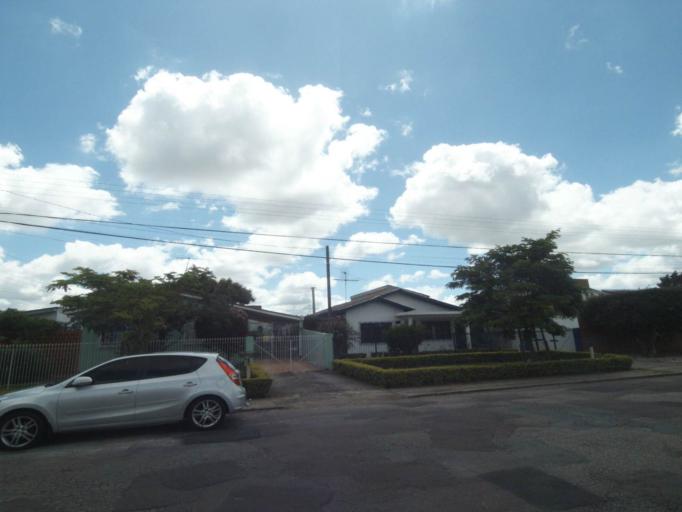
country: BR
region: Parana
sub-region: Pinhais
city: Pinhais
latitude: -25.4373
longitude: -49.2142
